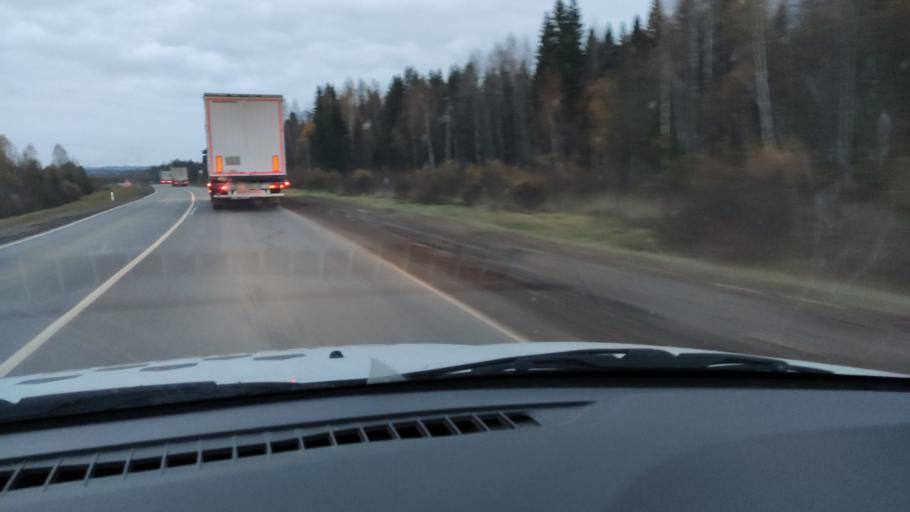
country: RU
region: Kirov
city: Kostino
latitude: 58.8554
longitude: 53.1966
